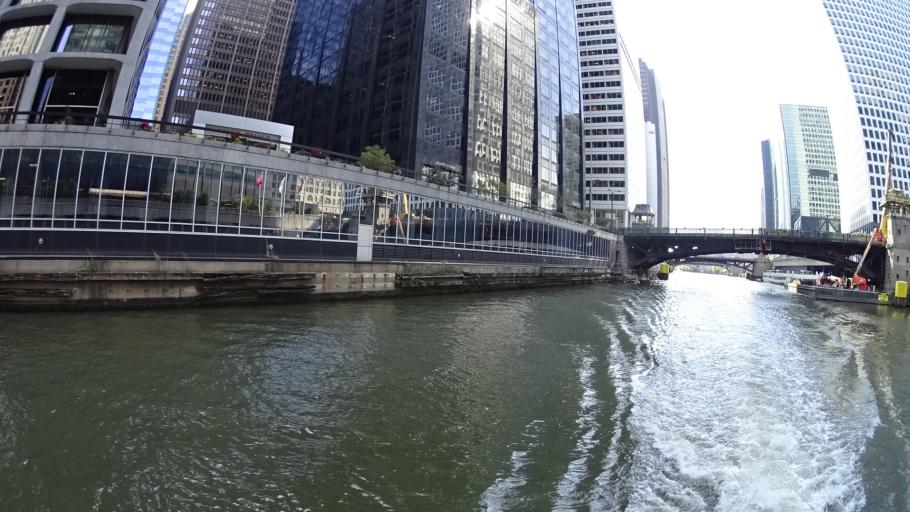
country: US
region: Illinois
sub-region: Cook County
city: Chicago
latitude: 41.8799
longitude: -87.6380
